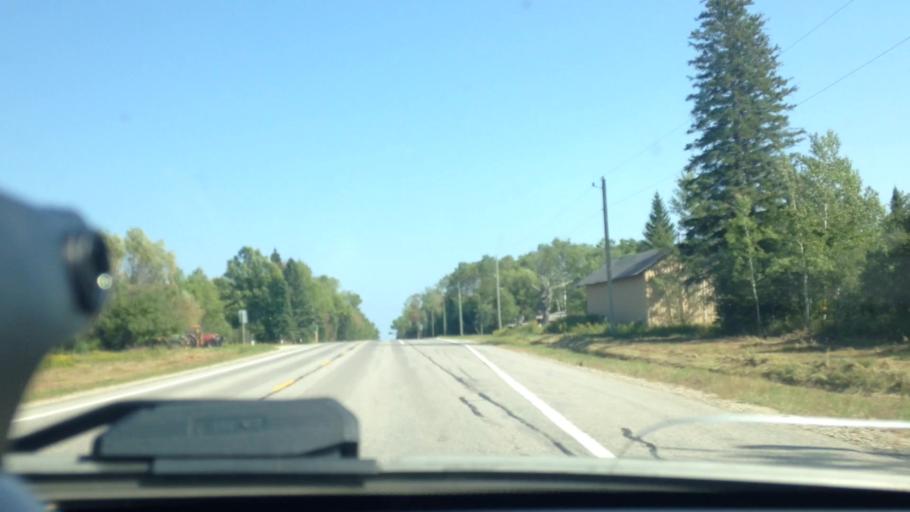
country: US
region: Michigan
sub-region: Luce County
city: Newberry
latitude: 46.3034
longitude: -85.3652
